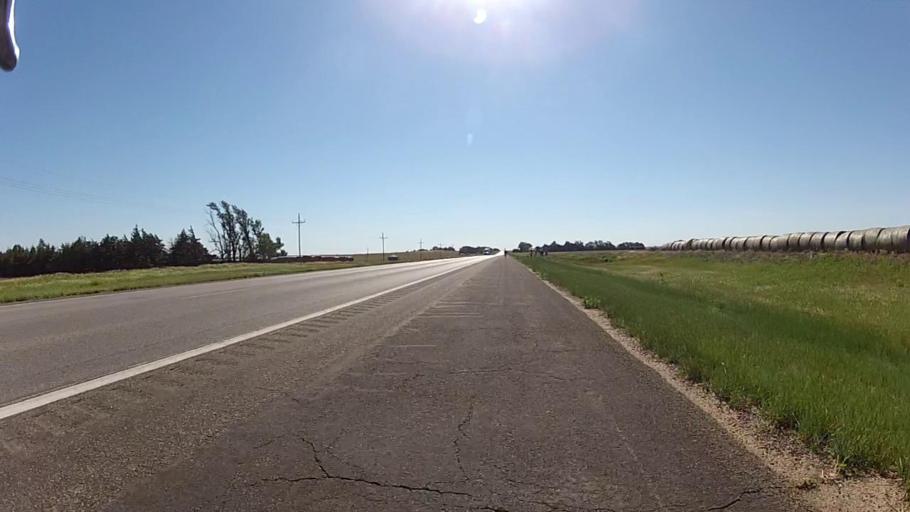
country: US
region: Kansas
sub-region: Kiowa County
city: Greensburg
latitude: 37.5864
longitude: -99.5919
